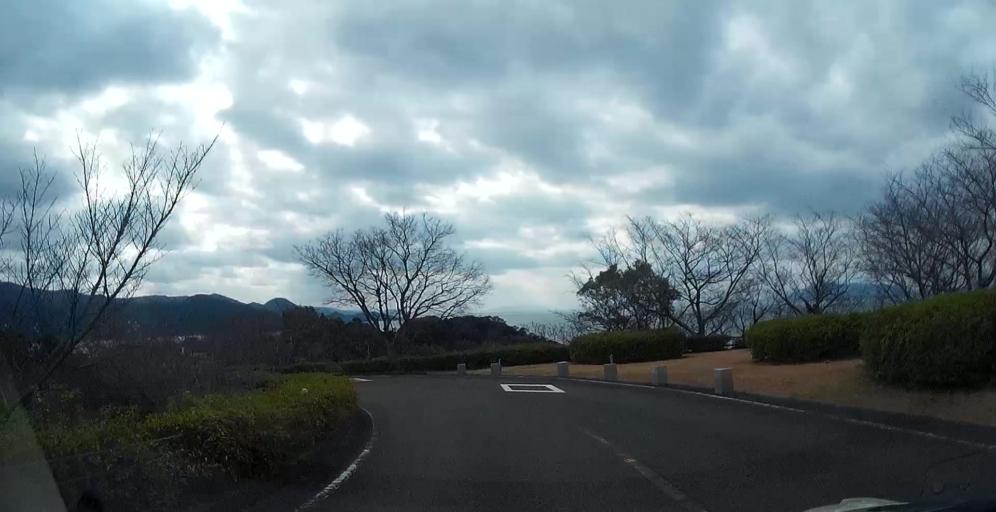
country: JP
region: Kumamoto
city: Minamata
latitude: 32.3651
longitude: 130.4911
